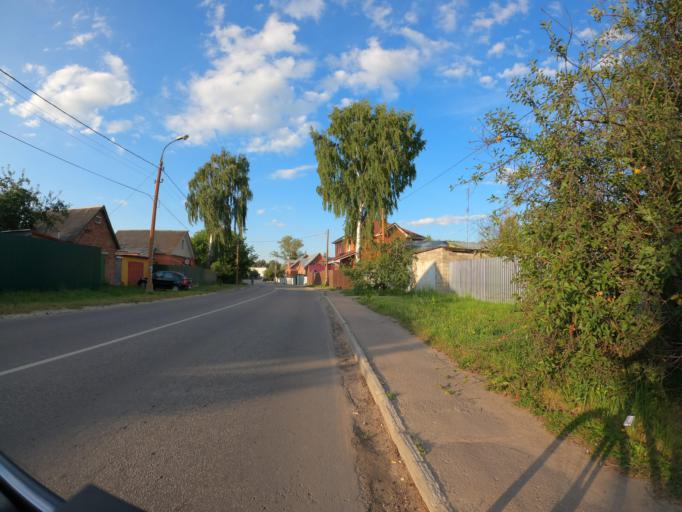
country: RU
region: Moskovskaya
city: Raduzhnyy
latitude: 55.1058
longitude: 38.7391
